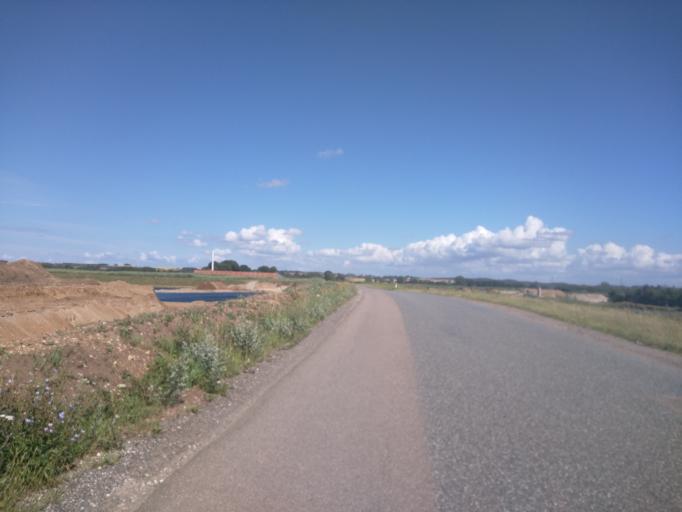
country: DK
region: Zealand
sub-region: Kalundborg Kommune
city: Svebolle
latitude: 55.6909
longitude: 11.2745
